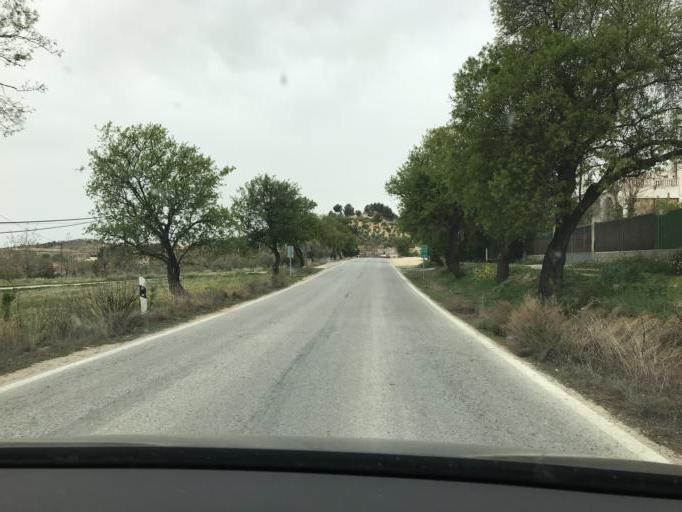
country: ES
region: Andalusia
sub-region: Provincia de Granada
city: Castril
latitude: 37.8175
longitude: -2.7608
